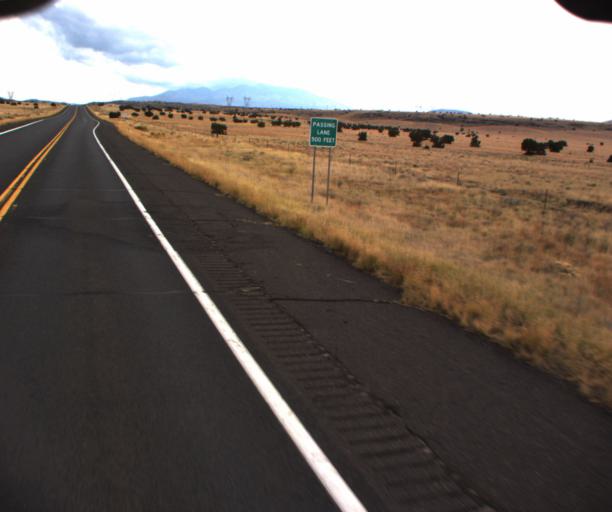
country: US
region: Arizona
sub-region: Coconino County
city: Flagstaff
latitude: 35.5502
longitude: -111.5368
